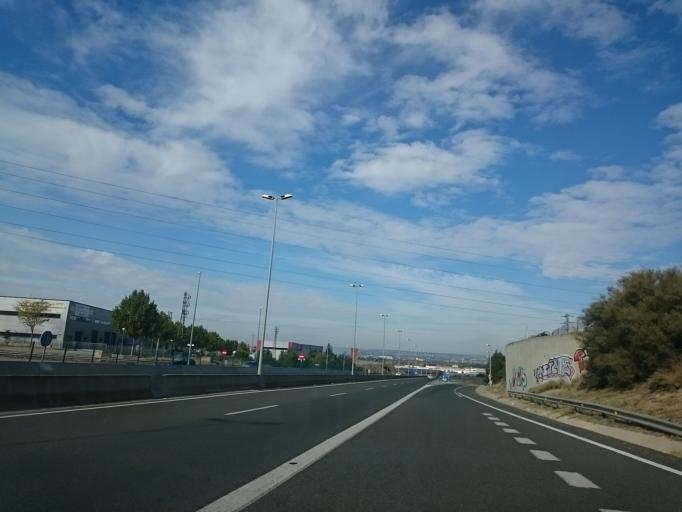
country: ES
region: Catalonia
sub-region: Provincia de Lleida
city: Alcoletge
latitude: 41.6155
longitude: 0.6694
